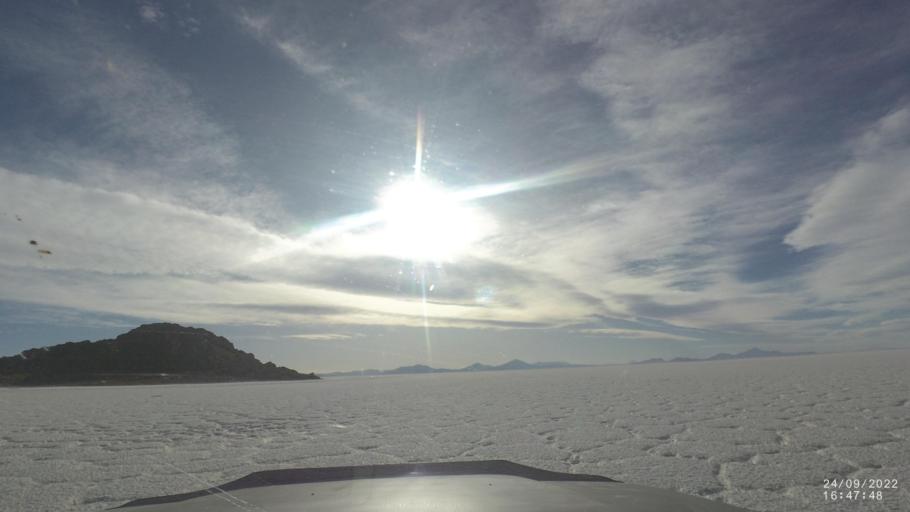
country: BO
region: Potosi
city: Colchani
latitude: -20.1318
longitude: -67.8073
